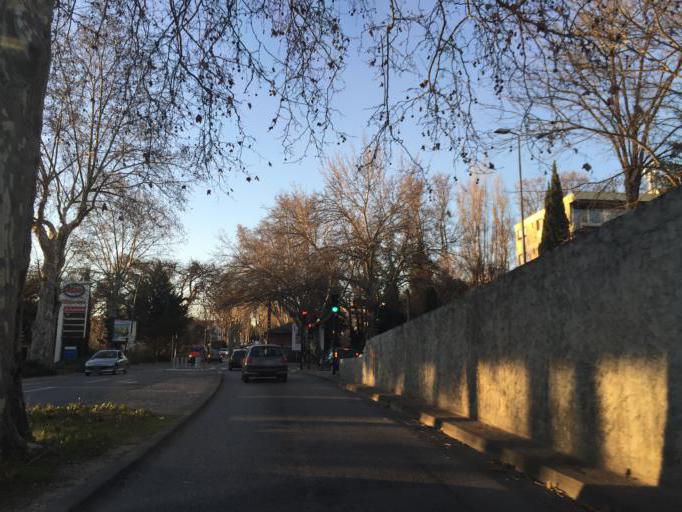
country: FR
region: Provence-Alpes-Cote d'Azur
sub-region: Departement des Bouches-du-Rhone
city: Aix-en-Provence
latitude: 43.5178
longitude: 5.4647
